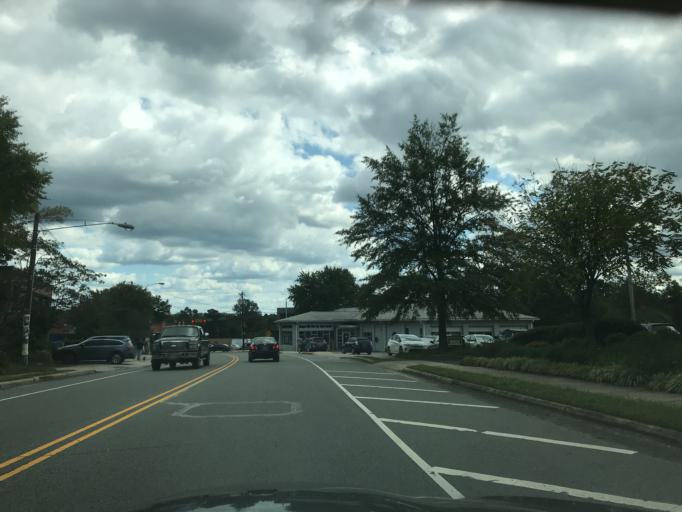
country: US
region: North Carolina
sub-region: Orange County
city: Carrboro
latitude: 35.9107
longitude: -79.0761
